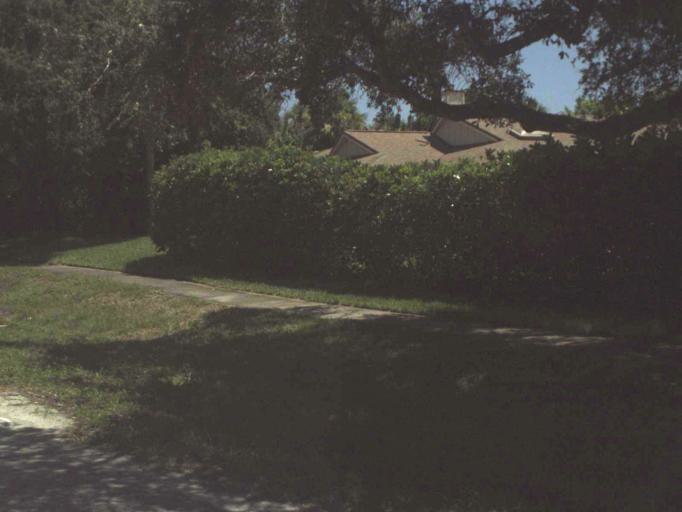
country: US
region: Florida
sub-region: Indian River County
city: Vero Beach
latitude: 27.6624
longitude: -80.3616
